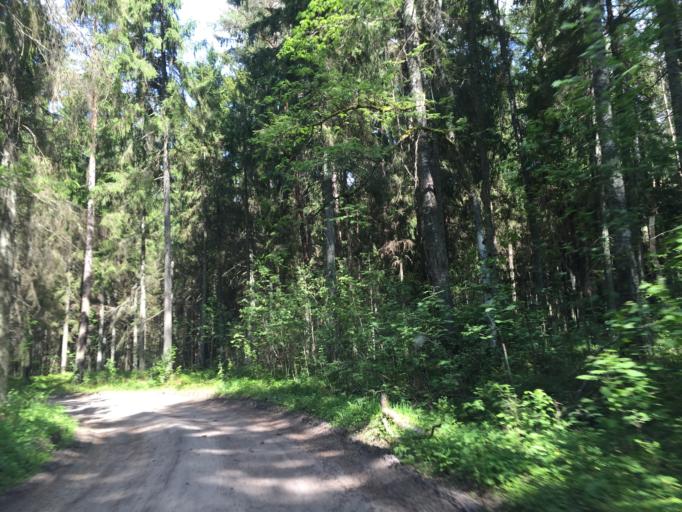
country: LV
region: Baldone
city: Baldone
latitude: 56.7828
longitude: 24.4219
